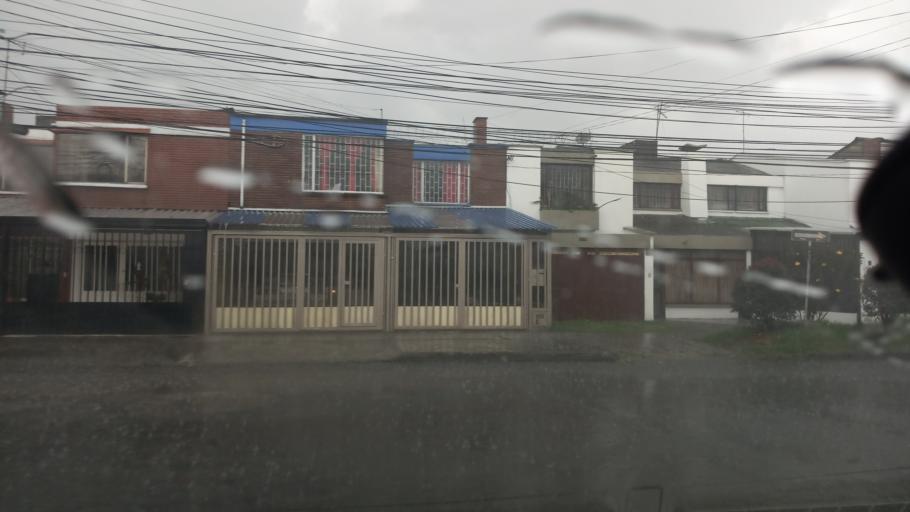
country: CO
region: Bogota D.C.
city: Bogota
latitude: 4.6636
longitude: -74.1238
